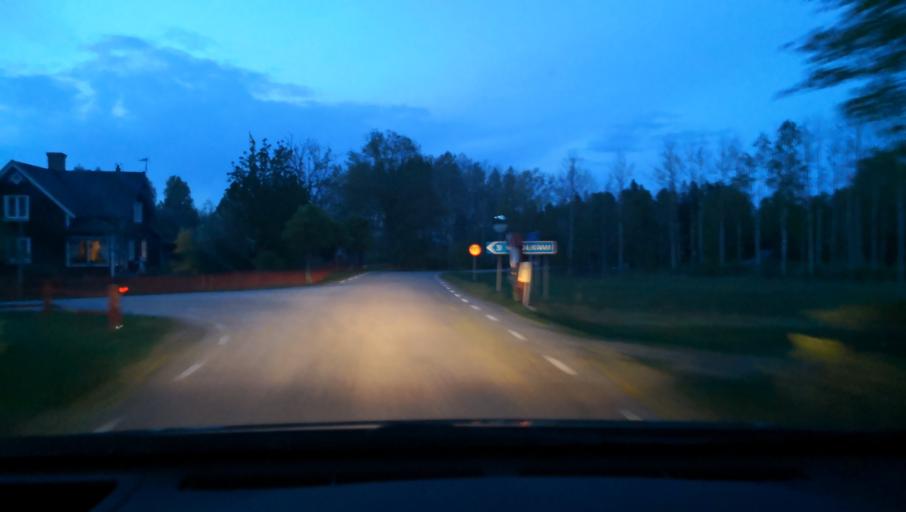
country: SE
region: OErebro
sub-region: Orebro Kommun
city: Vintrosa
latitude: 59.1807
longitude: 15.0203
